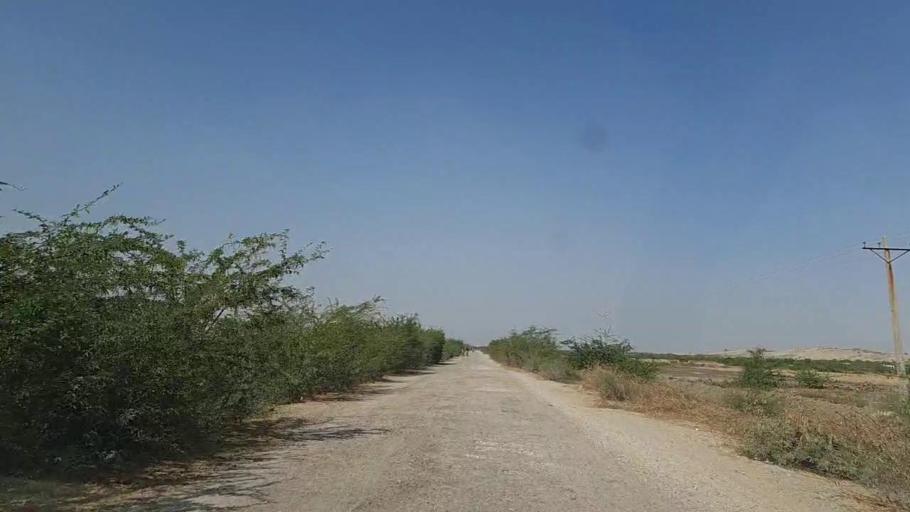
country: PK
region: Sindh
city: Naukot
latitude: 24.6251
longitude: 69.2889
